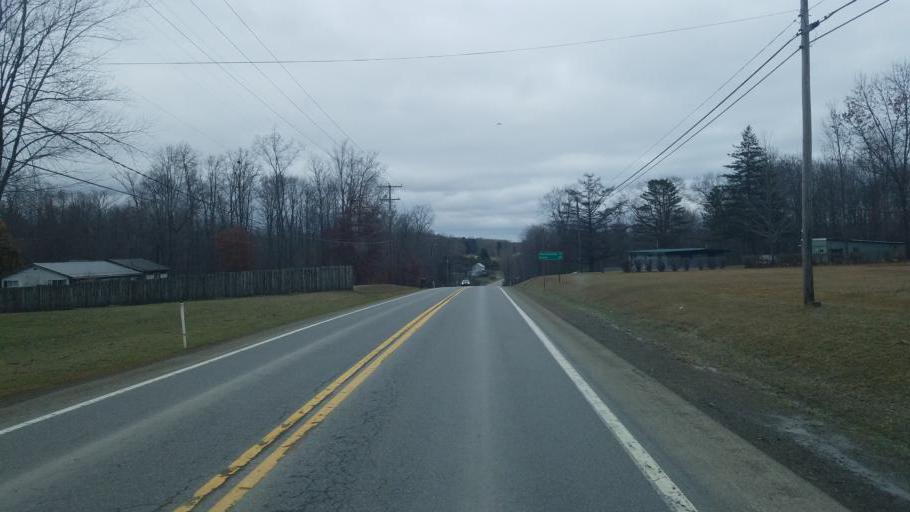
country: US
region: Pennsylvania
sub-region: Clarion County
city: Clarion
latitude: 41.3713
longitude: -79.3019
